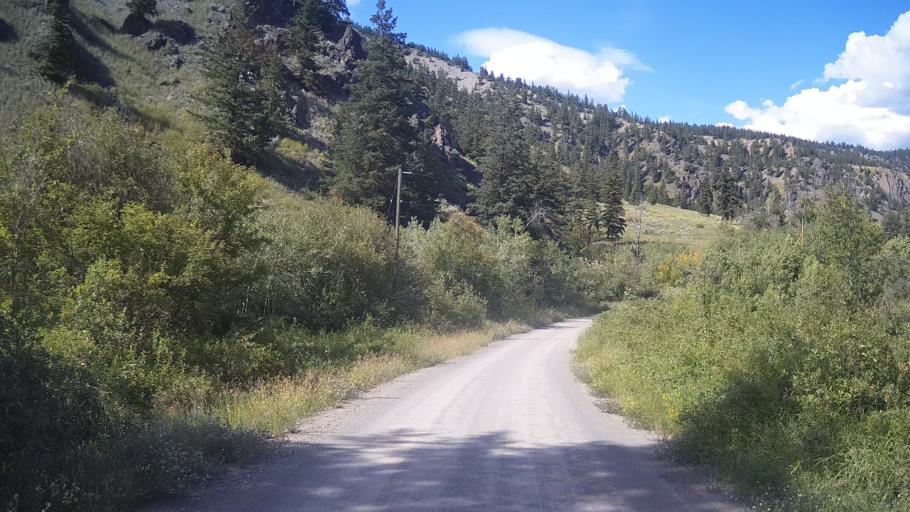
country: CA
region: British Columbia
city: Lillooet
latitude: 51.2342
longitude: -122.0521
